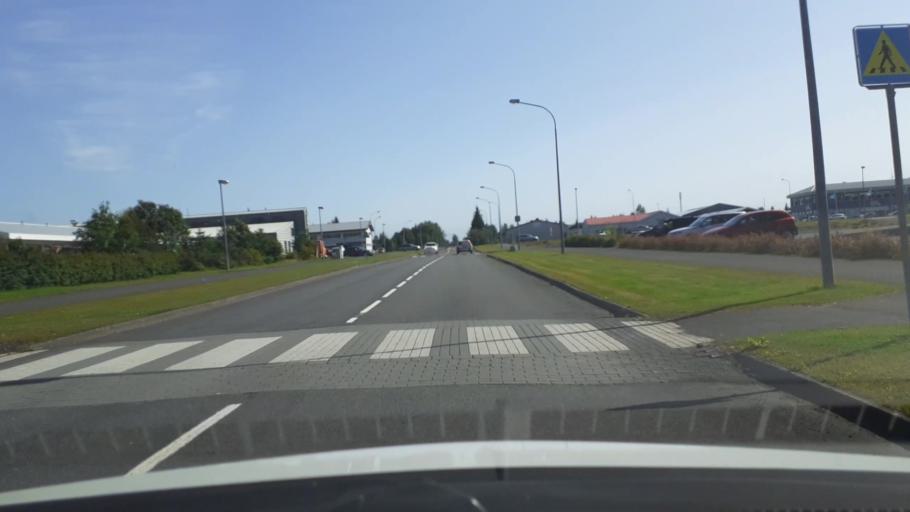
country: IS
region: South
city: Selfoss
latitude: 63.9352
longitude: -21.0141
